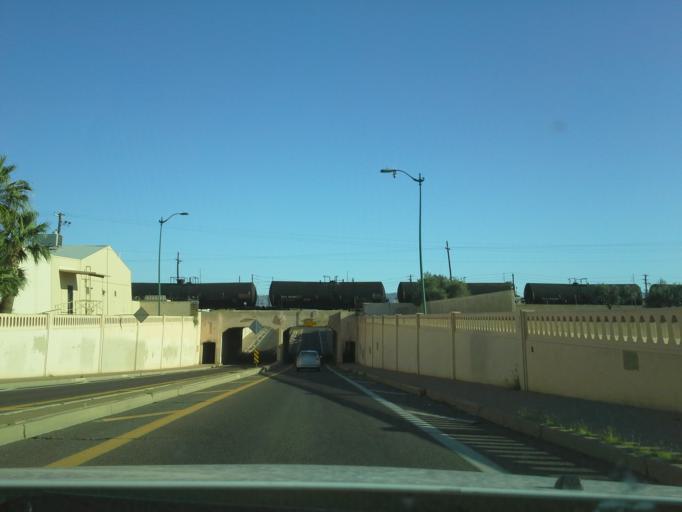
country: US
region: Arizona
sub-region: Maricopa County
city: Phoenix
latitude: 33.4449
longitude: -112.0959
